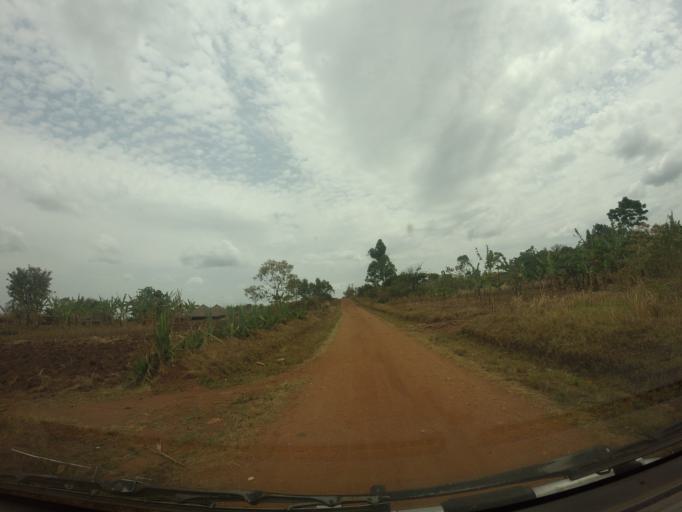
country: UG
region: Northern Region
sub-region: Arua District
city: Arua
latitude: 2.8235
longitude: 30.9044
